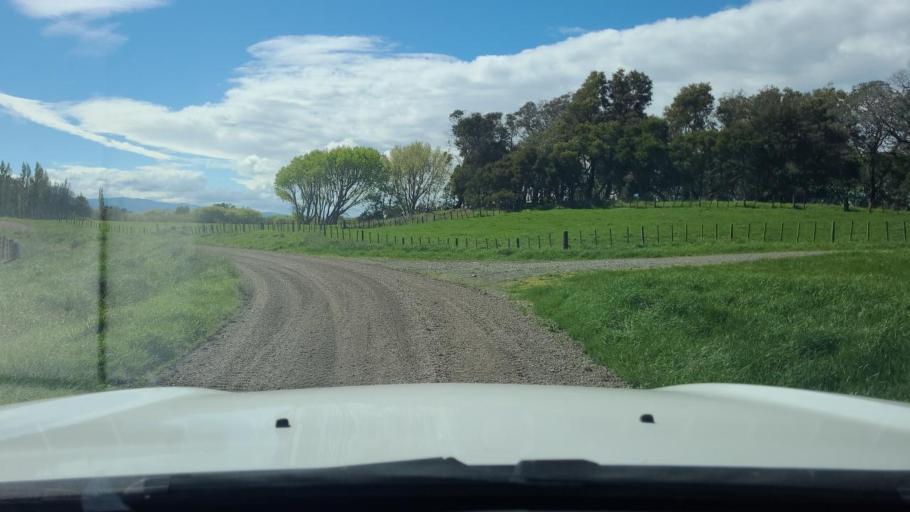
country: NZ
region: Wellington
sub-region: Upper Hutt City
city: Upper Hutt
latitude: -41.2623
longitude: 175.2783
